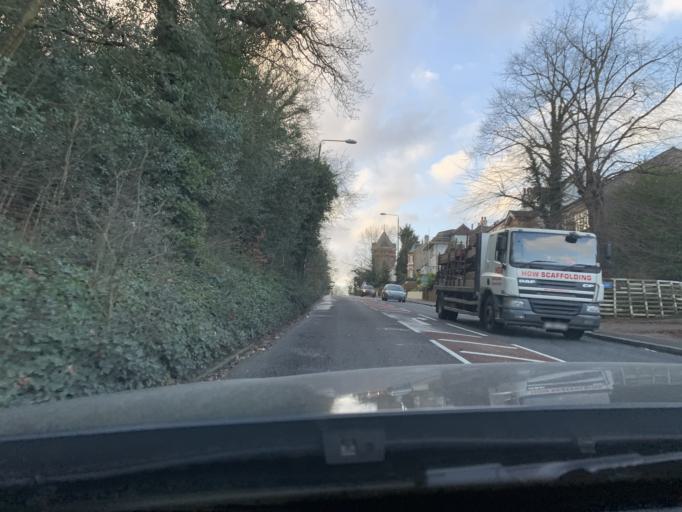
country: GB
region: England
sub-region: Greater London
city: Woolwich
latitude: 51.4684
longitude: 0.0719
